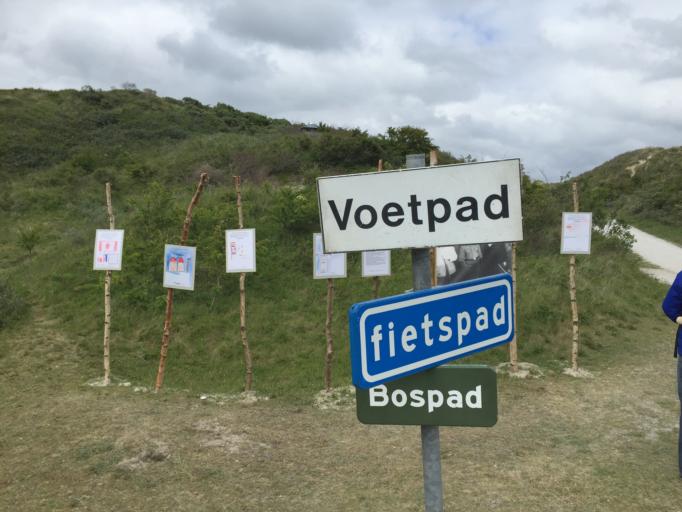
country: NL
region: Friesland
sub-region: Gemeente Schiermonnikoog
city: Schiermonnikoog
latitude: 53.4925
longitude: 6.1547
